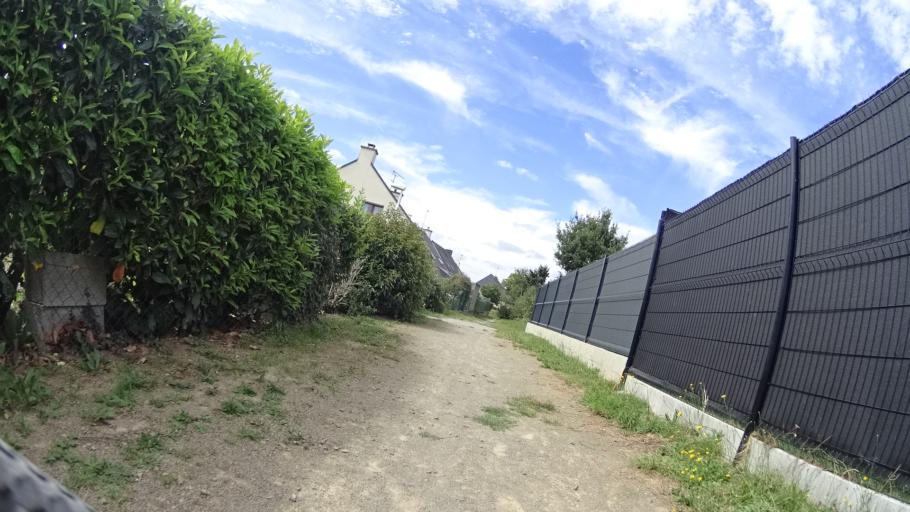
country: FR
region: Brittany
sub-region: Departement d'Ille-et-Vilaine
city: La Meziere
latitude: 48.2210
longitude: -1.7511
